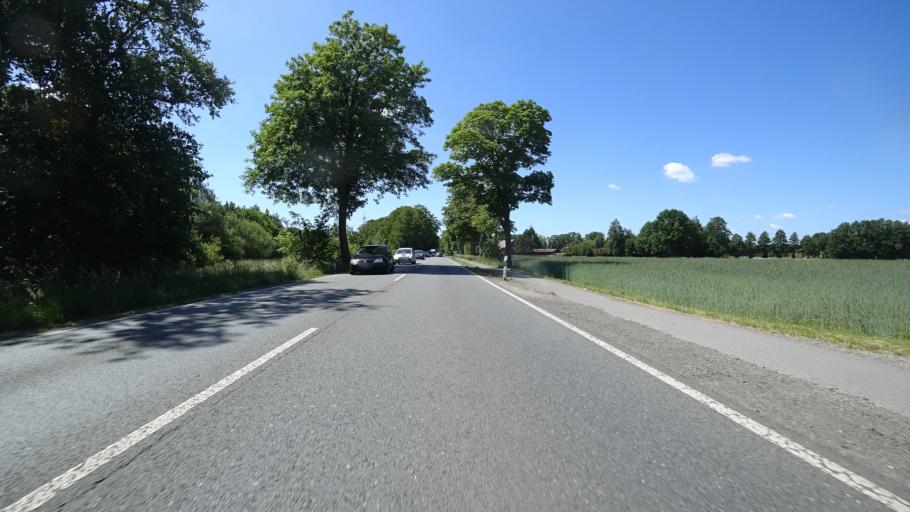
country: DE
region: North Rhine-Westphalia
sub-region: Regierungsbezirk Detmold
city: Guetersloh
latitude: 51.9339
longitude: 8.4155
